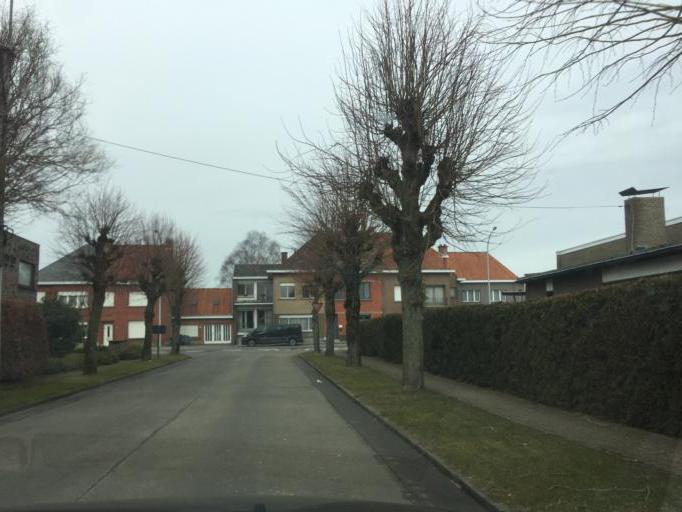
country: BE
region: Flanders
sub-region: Provincie West-Vlaanderen
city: Roeselare
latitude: 50.9371
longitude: 3.1104
